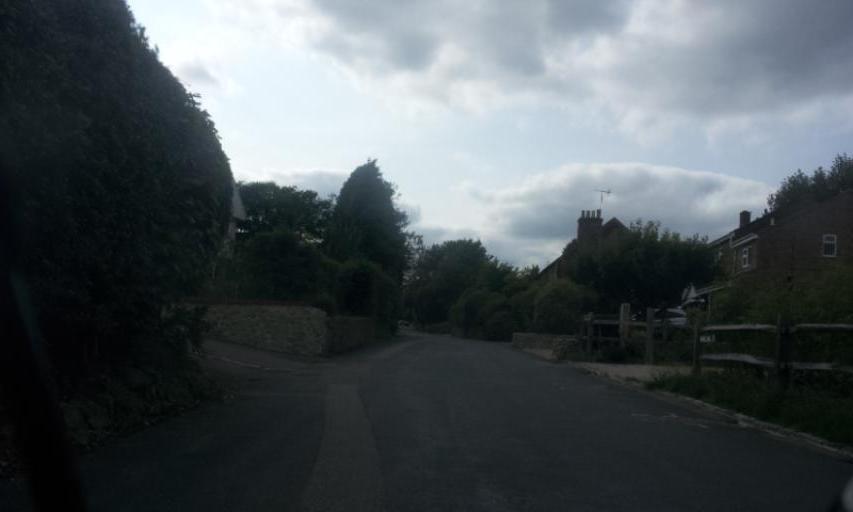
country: GB
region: England
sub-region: Kent
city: Borough Green
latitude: 51.2579
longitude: 0.3029
